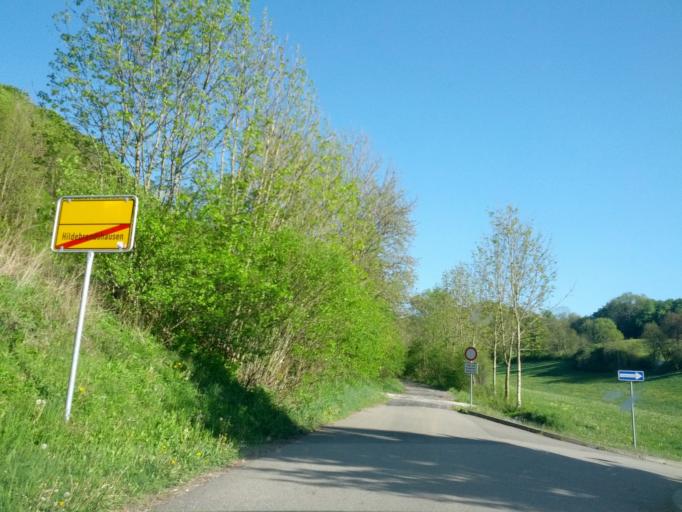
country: DE
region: Thuringia
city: Katharinenberg
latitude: 51.1976
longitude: 10.2213
